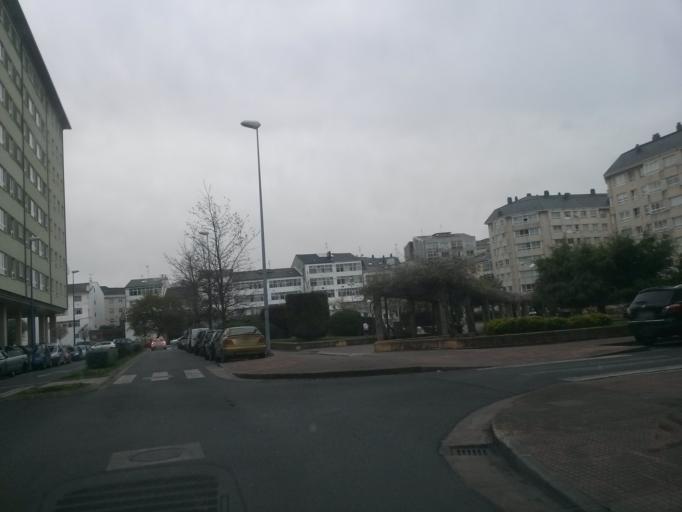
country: ES
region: Galicia
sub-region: Provincia de Lugo
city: Lugo
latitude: 43.0226
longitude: -7.5671
